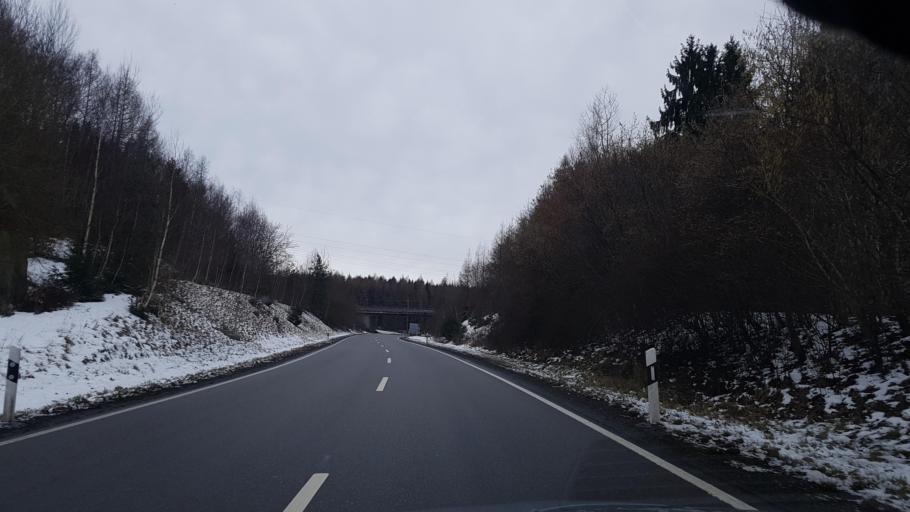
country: DE
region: Bavaria
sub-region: Upper Bavaria
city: Kirchdorf
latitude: 48.1598
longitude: 12.2003
